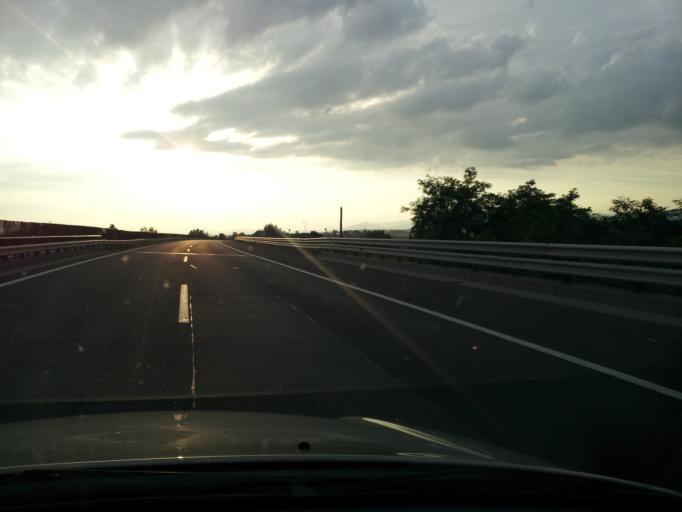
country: HU
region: Heves
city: Karacsond
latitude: 47.7078
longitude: 20.0139
